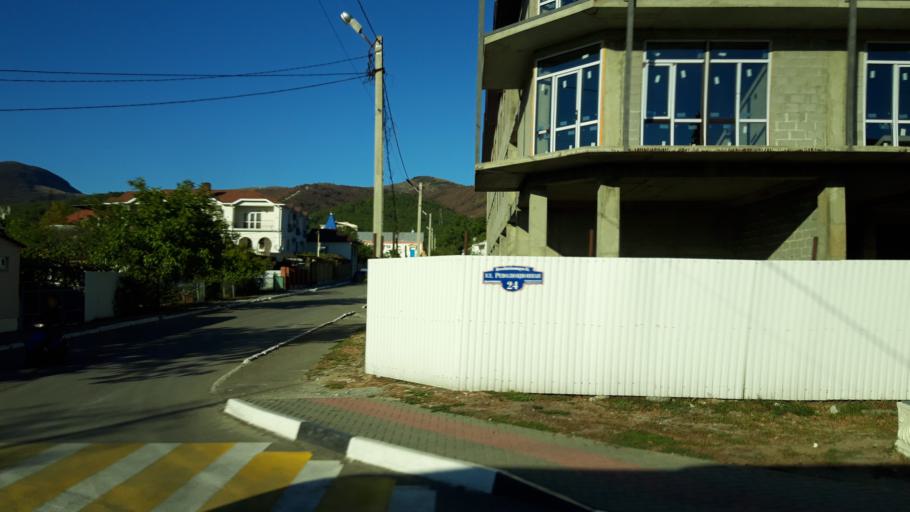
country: RU
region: Krasnodarskiy
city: Kabardinka
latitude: 44.6484
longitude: 37.9485
